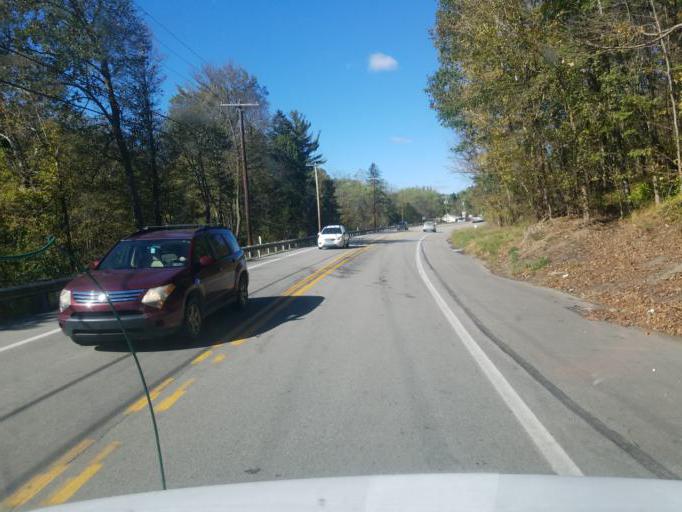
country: US
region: Pennsylvania
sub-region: Westmoreland County
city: Ligonier
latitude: 40.2333
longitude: -79.2269
